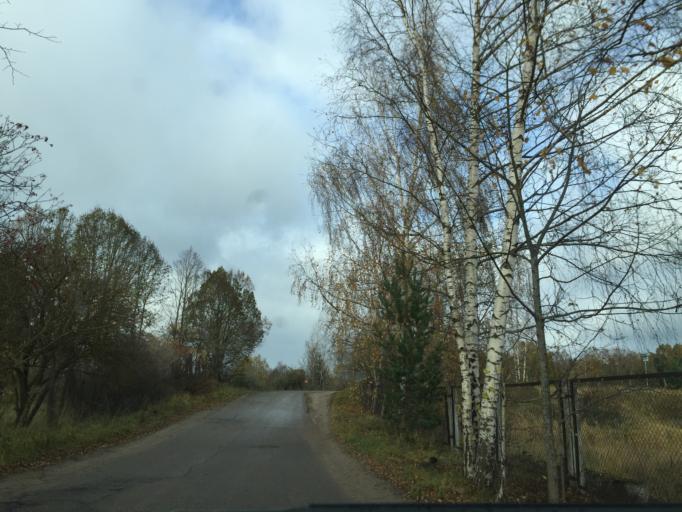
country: LV
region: Tukuma Rajons
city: Tukums
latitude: 56.9621
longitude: 23.1111
